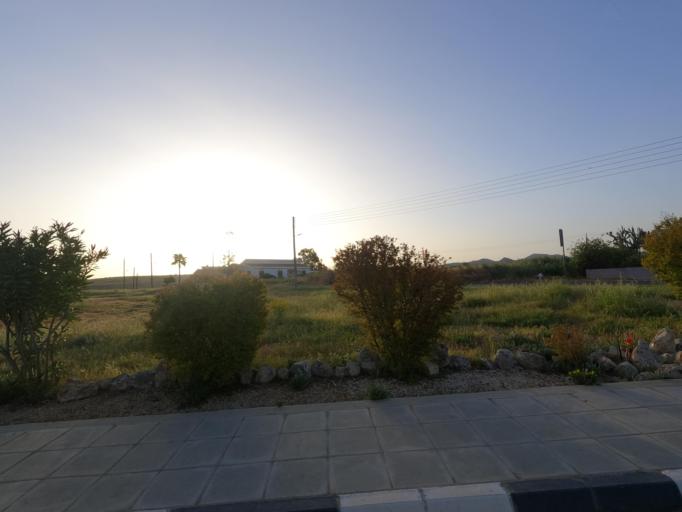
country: CY
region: Lefkosia
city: Astromeritis
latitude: 35.0813
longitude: 33.0160
